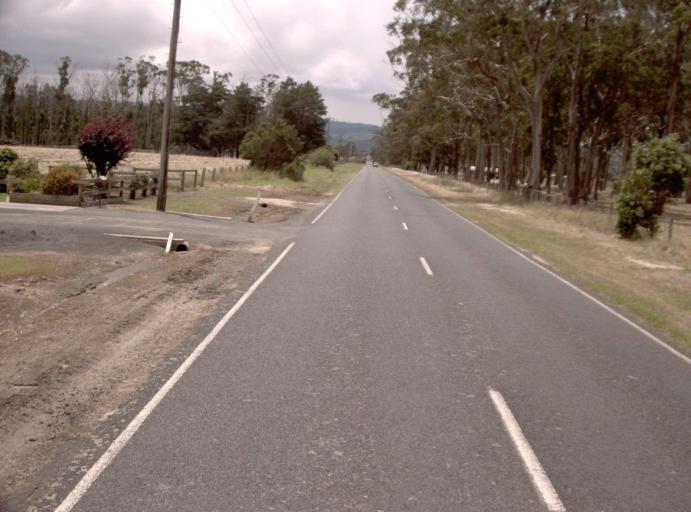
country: AU
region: Victoria
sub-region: Latrobe
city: Traralgon
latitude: -38.5356
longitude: 146.6577
